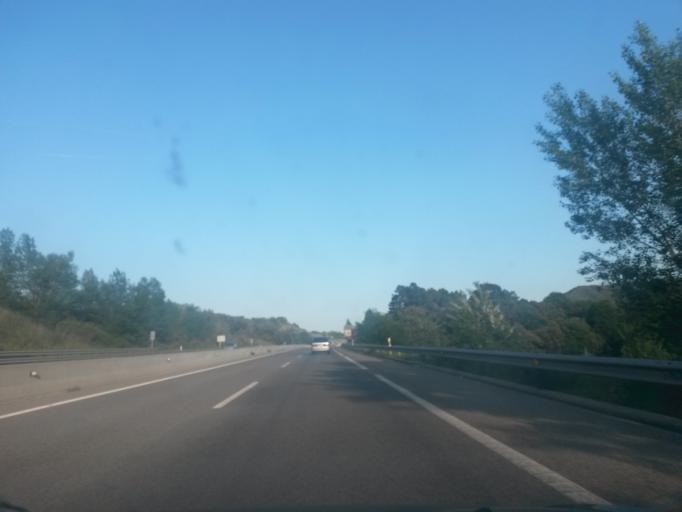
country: ES
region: Catalonia
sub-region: Provincia de Girona
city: Argelaguer
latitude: 42.2148
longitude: 2.6576
